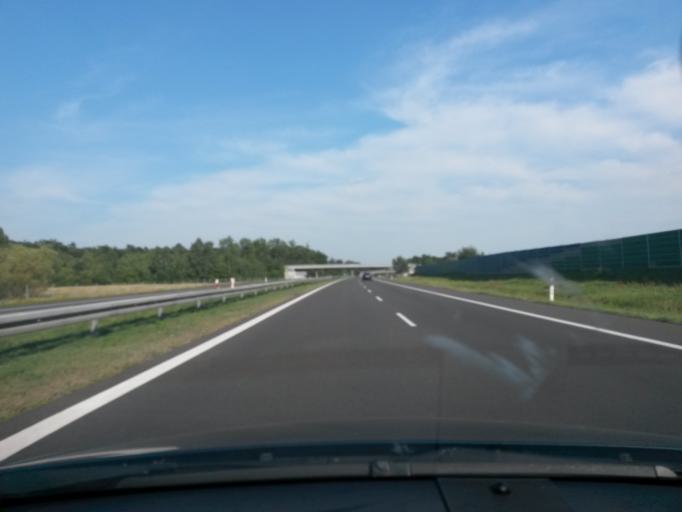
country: PL
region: Greater Poland Voivodeship
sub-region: Powiat wrzesinski
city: Wrzesnia
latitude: 52.3086
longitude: 17.5880
